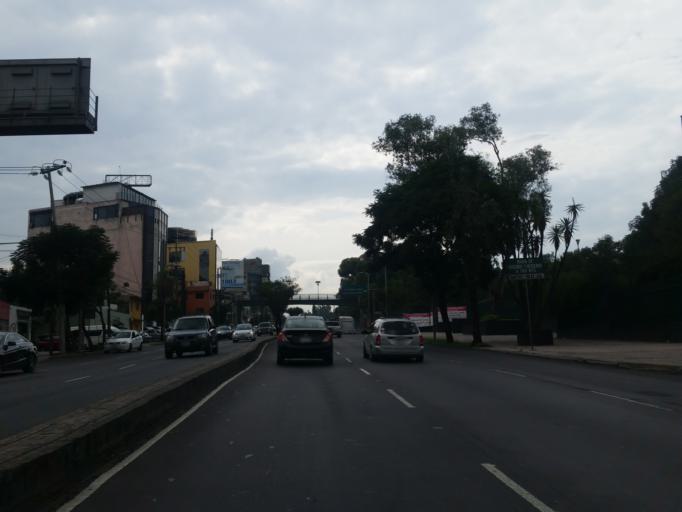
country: MX
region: Mexico City
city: Polanco
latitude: 19.4083
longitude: -99.1988
